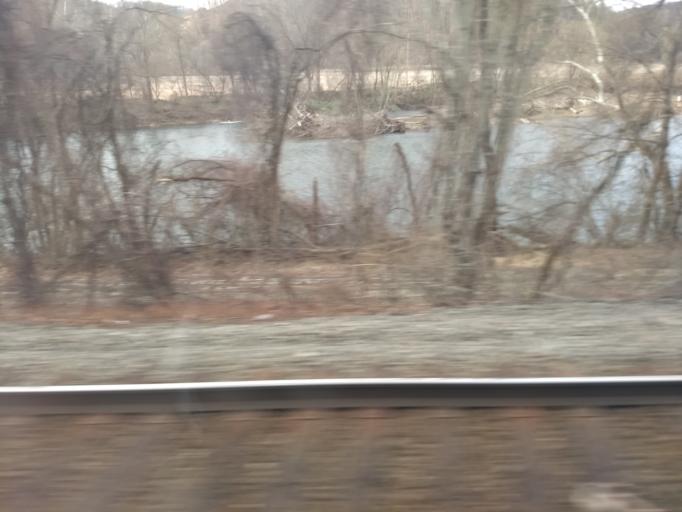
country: US
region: Pennsylvania
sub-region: Huntingdon County
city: Huntingdon
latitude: 40.4751
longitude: -77.9961
